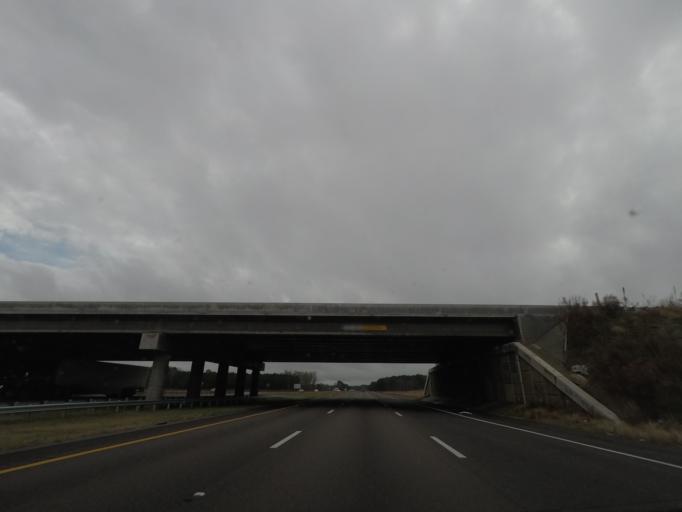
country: US
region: South Carolina
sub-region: Orangeburg County
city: Holly Hill
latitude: 33.4625
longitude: -80.4784
